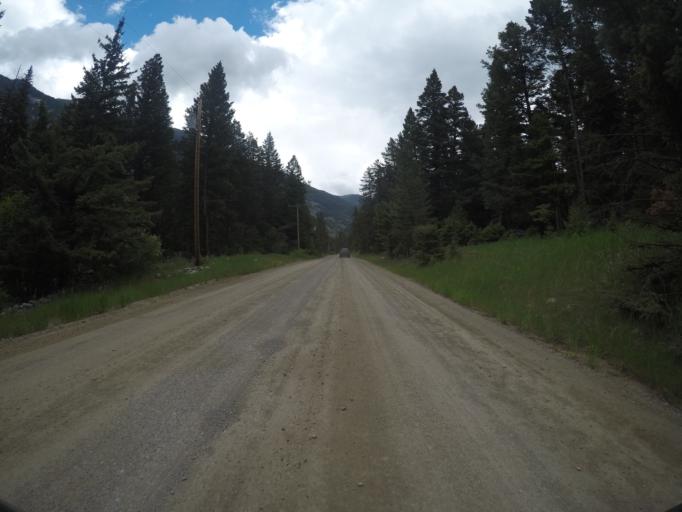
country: US
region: Montana
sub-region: Park County
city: Livingston
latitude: 45.4910
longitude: -110.2225
